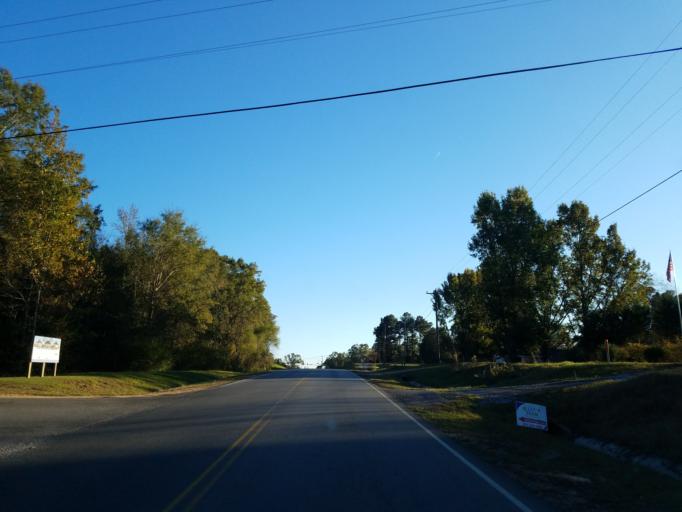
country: US
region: Mississippi
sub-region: Lamar County
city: Arnold Line
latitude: 31.3421
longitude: -89.3989
